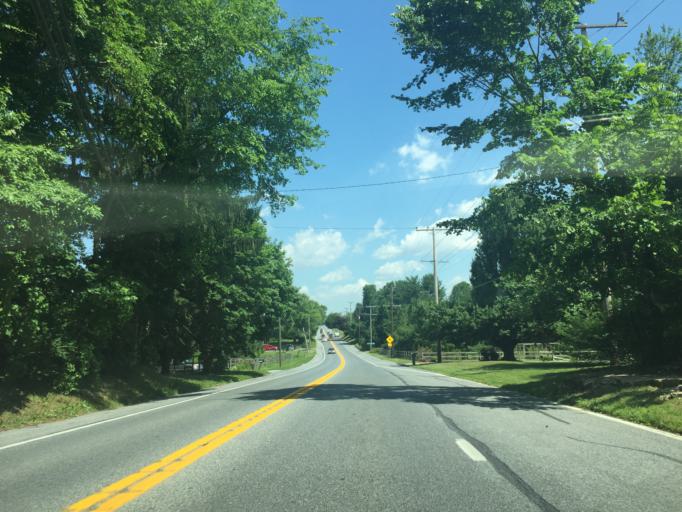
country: US
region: Maryland
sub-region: Baltimore County
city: Reisterstown
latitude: 39.4938
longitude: -76.8308
